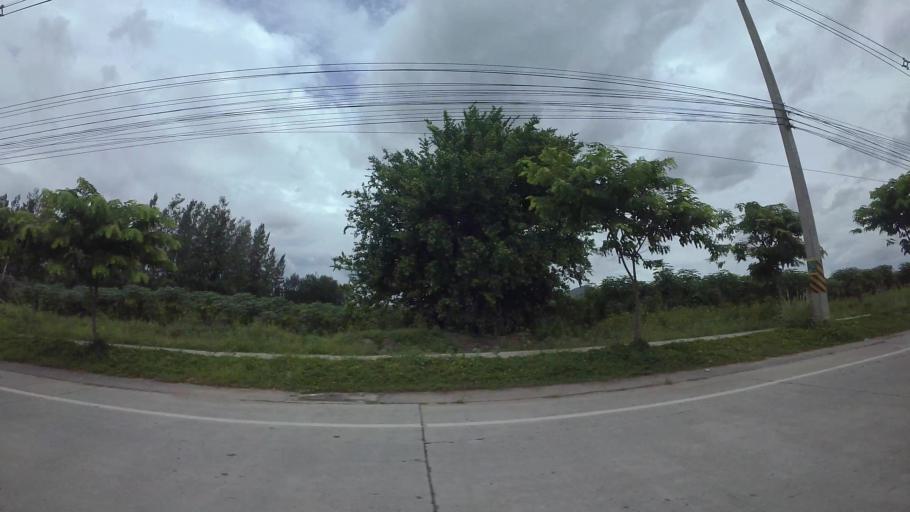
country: TH
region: Chon Buri
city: Si Racha
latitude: 13.1580
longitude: 100.9843
